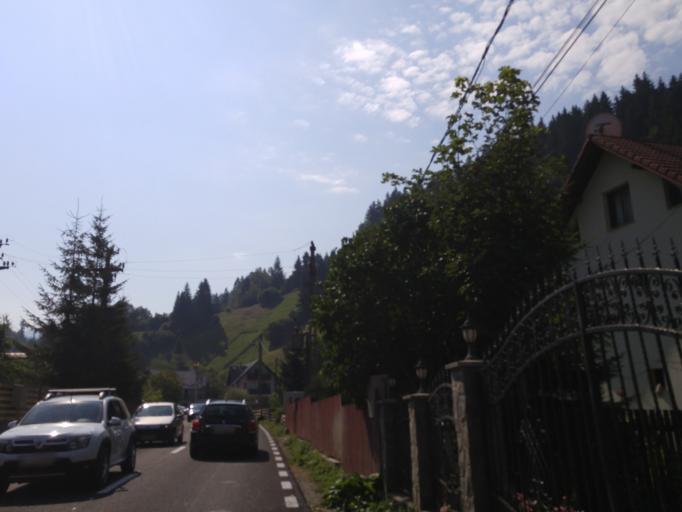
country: RO
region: Brasov
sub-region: Comuna Fundata
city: Fundata
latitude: 45.4604
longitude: 25.3089
